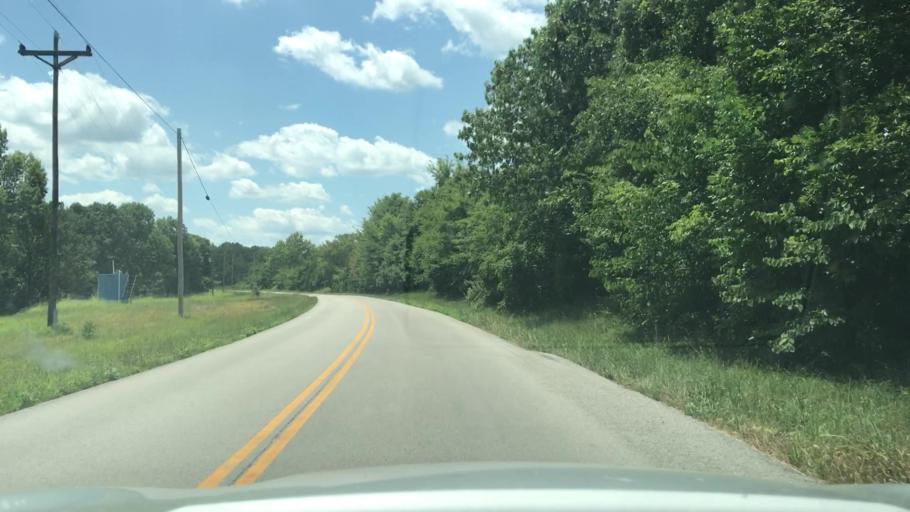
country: US
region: Kentucky
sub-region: Hopkins County
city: Nortonville
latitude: 37.1137
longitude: -87.3300
